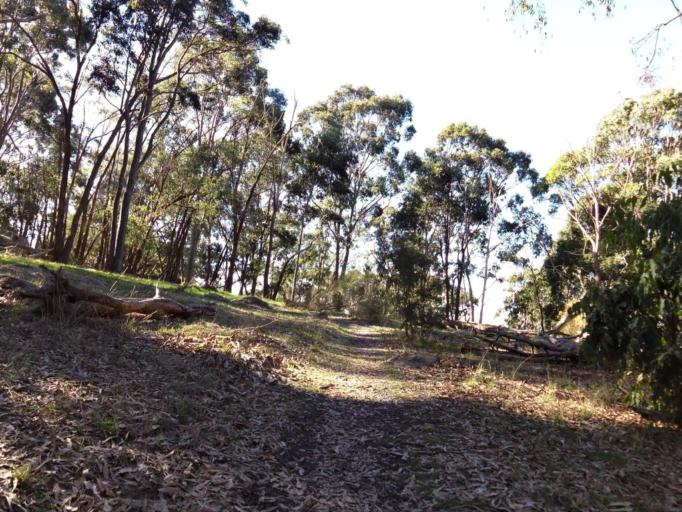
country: AU
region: Victoria
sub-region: Yarra Ranges
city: Lysterfield
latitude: -37.9447
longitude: 145.2791
